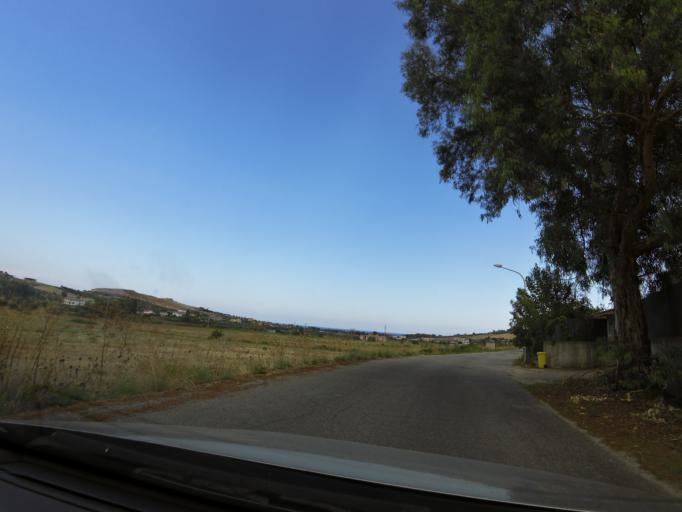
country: IT
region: Calabria
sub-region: Provincia di Reggio Calabria
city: Monasterace
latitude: 38.4252
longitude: 16.5369
